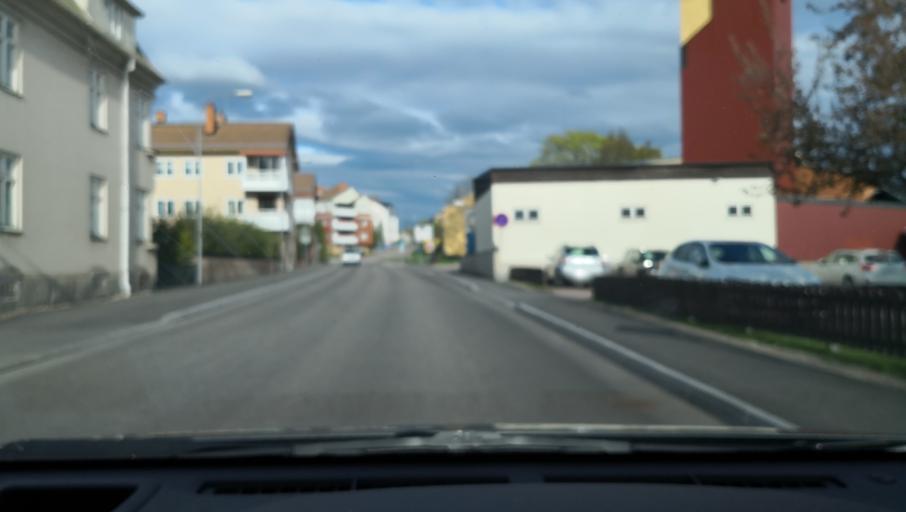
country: SE
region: Dalarna
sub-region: Hedemora Kommun
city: Hedemora
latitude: 60.2782
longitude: 15.9801
